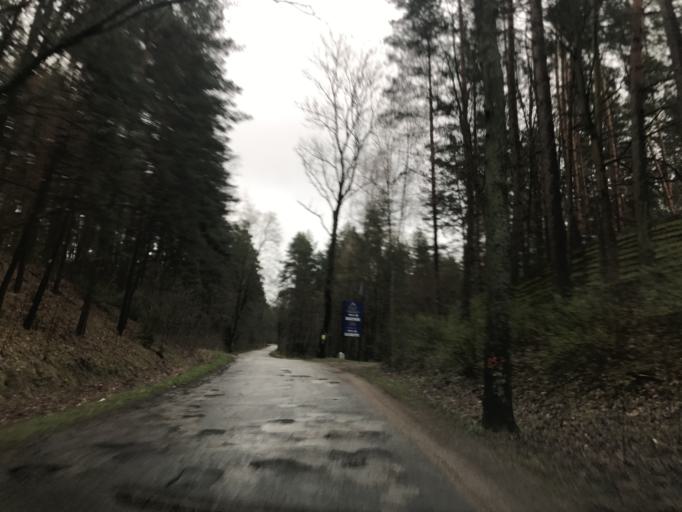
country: PL
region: Warmian-Masurian Voivodeship
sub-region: Powiat olsztynski
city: Stawiguda
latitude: 53.7167
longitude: 20.3718
